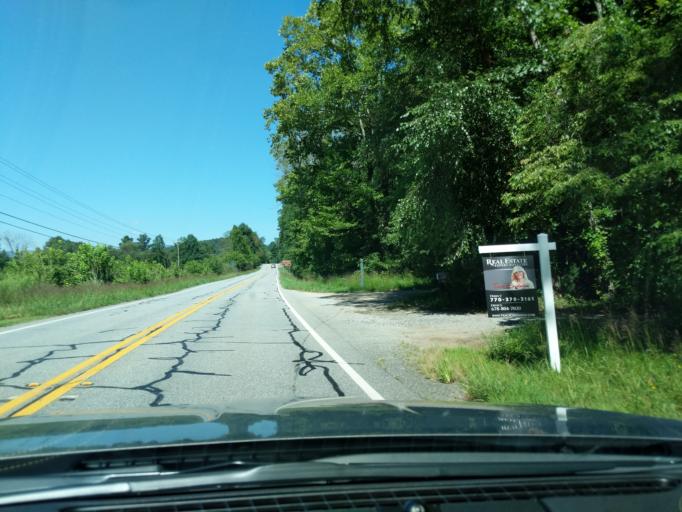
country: US
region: Georgia
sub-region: White County
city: Cleveland
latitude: 34.6775
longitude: -83.6643
